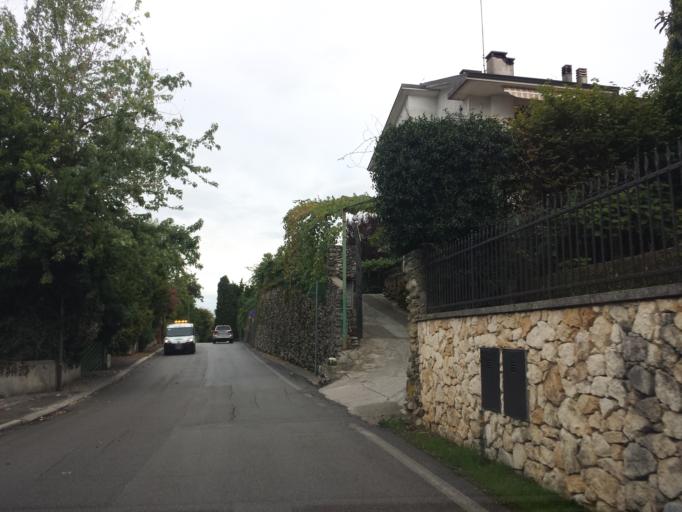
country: IT
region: Veneto
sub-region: Provincia di Vicenza
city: Arcugnano-Torri
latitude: 45.4979
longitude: 11.5368
